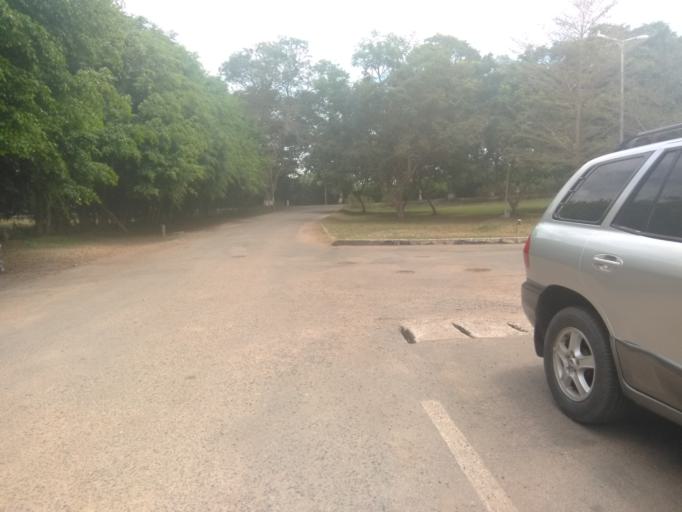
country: GH
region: Central
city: Cape Coast
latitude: 5.1173
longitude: -1.2885
